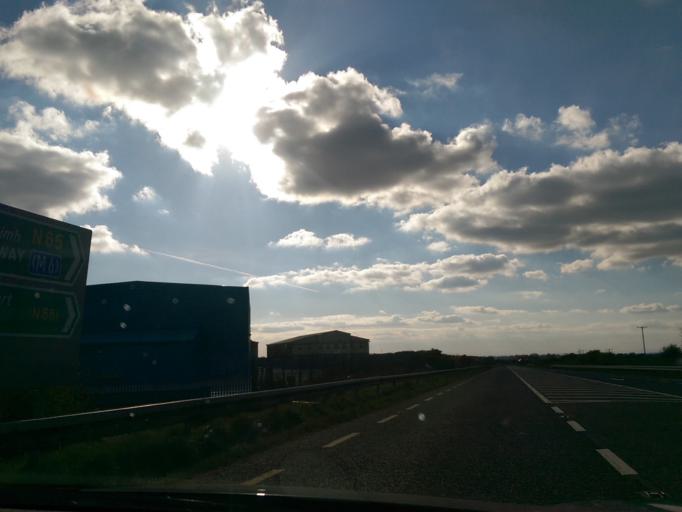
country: IE
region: Connaught
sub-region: County Galway
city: Loughrea
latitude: 53.2054
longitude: -8.5470
